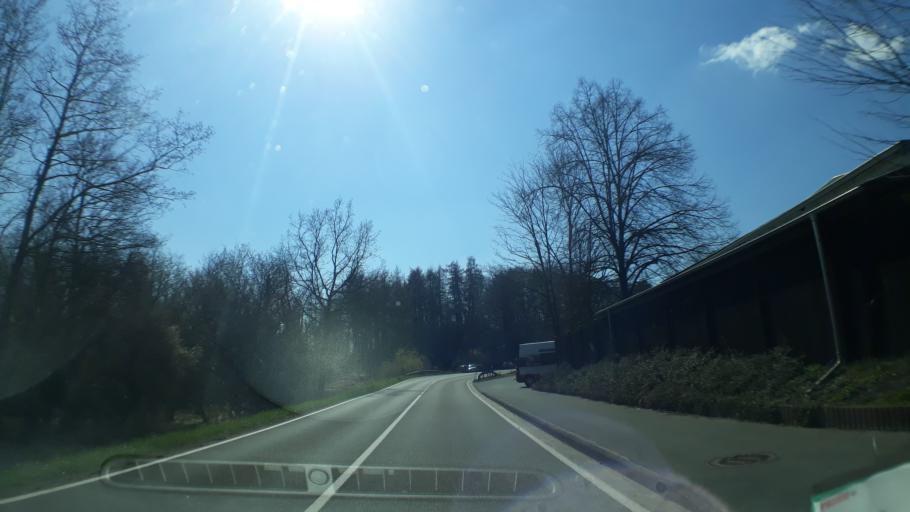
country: DE
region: North Rhine-Westphalia
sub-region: Regierungsbezirk Koln
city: Mechernich
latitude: 50.5925
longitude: 6.6737
